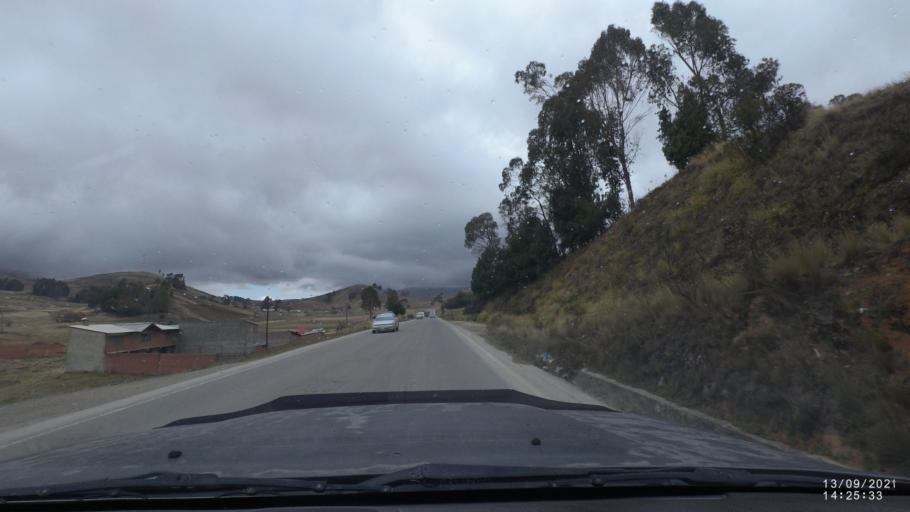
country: BO
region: Cochabamba
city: Colomi
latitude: -17.2972
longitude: -65.8699
